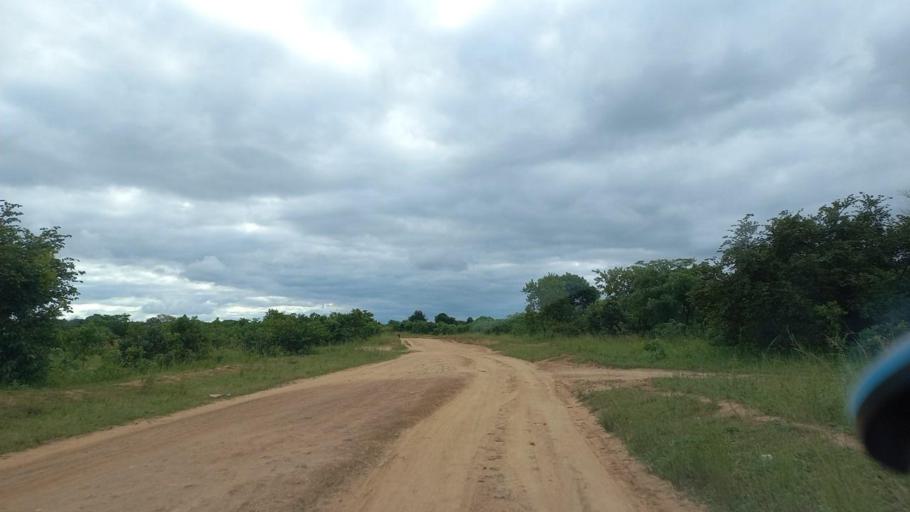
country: ZM
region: Lusaka
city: Chongwe
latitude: -15.4495
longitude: 28.8420
